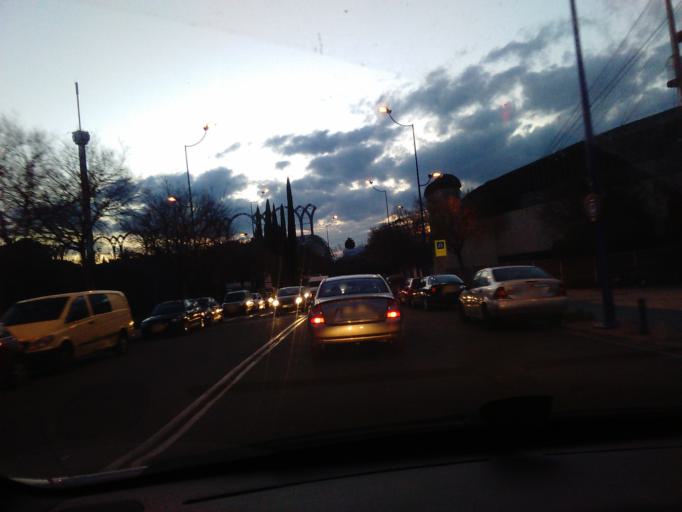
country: ES
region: Andalusia
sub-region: Provincia de Sevilla
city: Camas
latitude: 37.4052
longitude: -5.9995
